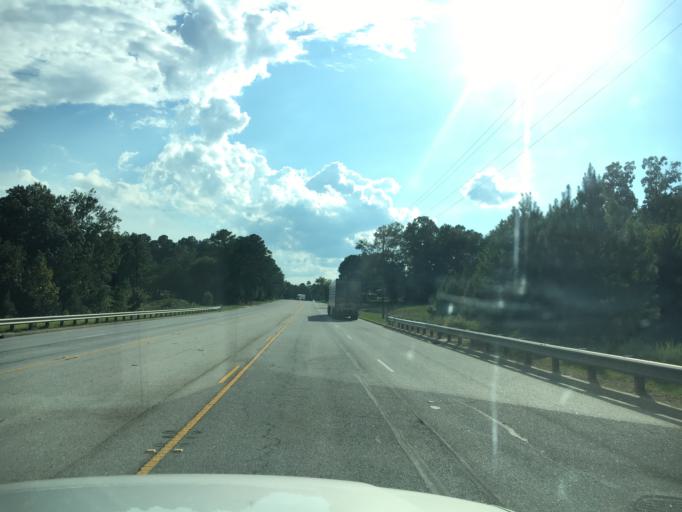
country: US
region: South Carolina
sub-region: Greenwood County
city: Ninety Six
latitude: 34.2892
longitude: -82.0404
